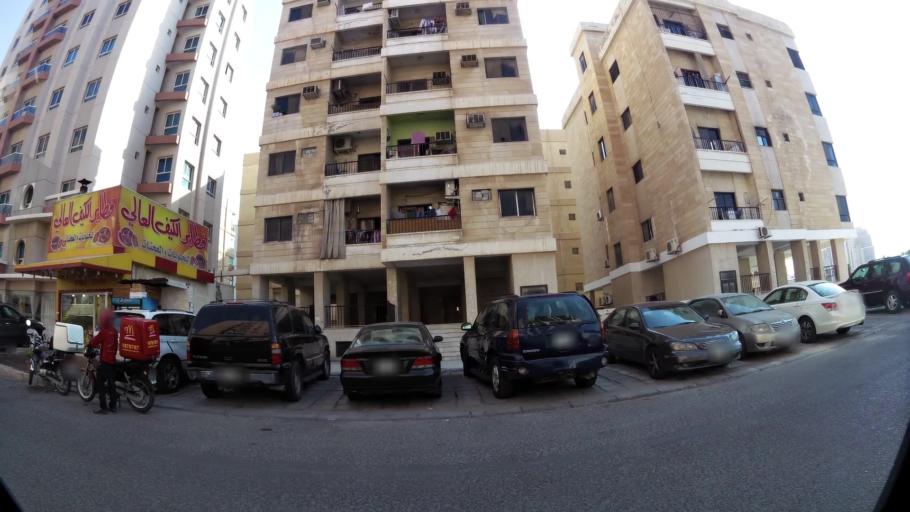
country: KW
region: Muhafazat Hawalli
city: As Salimiyah
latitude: 29.3413
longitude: 48.0925
